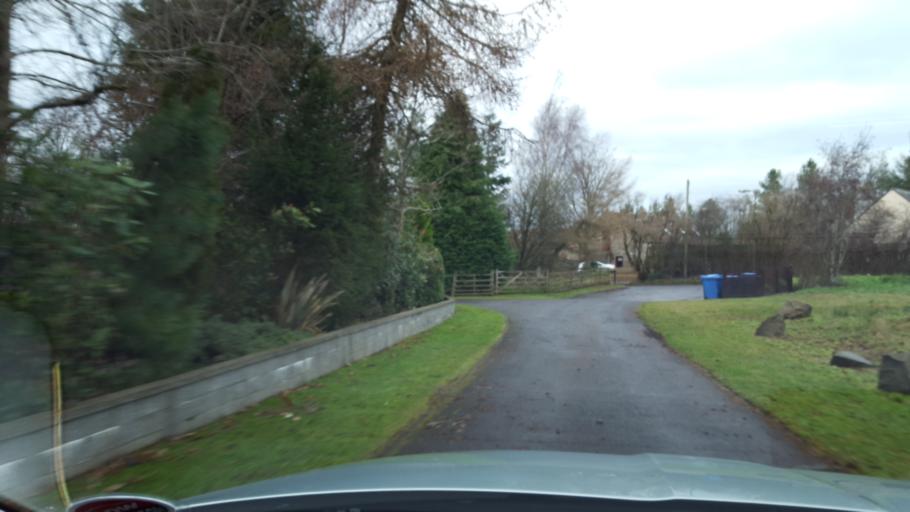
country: GB
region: Scotland
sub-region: West Lothian
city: Livingston
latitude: 55.8570
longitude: -3.5130
